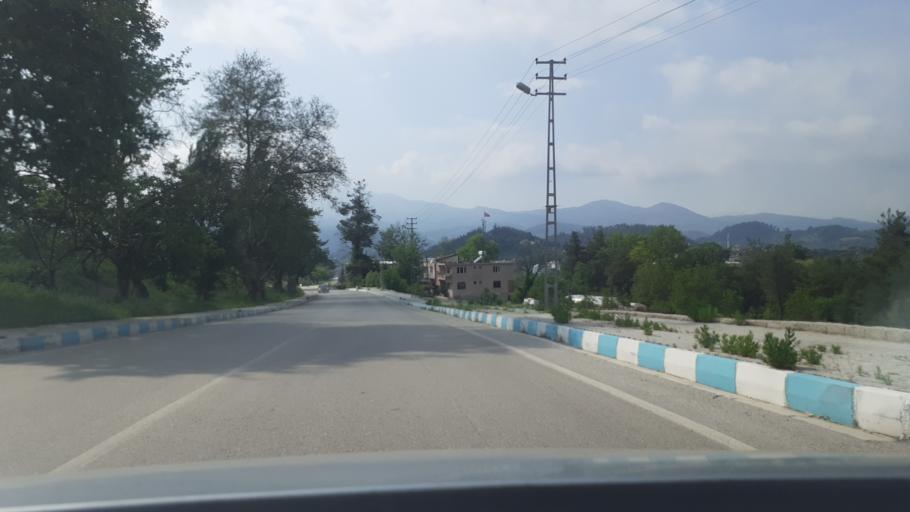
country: TR
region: Hatay
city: Yayladagi
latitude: 35.8970
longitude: 36.0764
